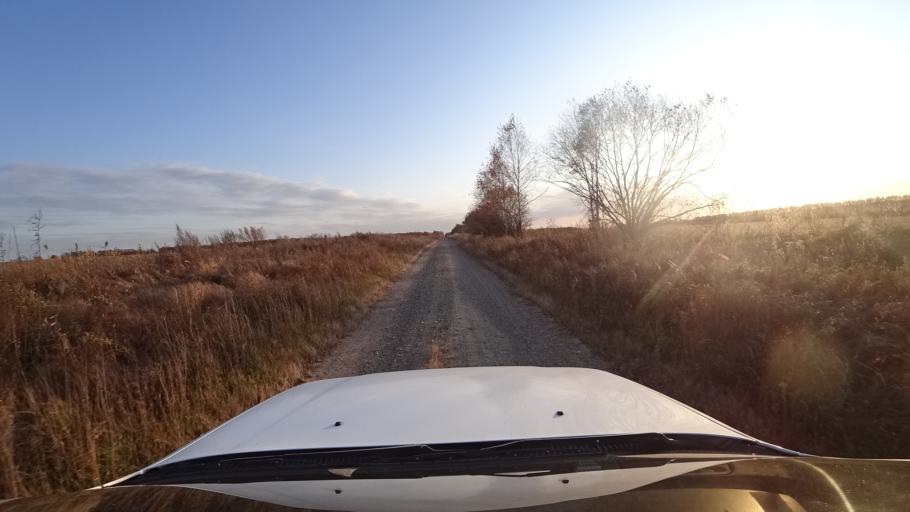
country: RU
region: Primorskiy
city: Lazo
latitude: 45.8125
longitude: 133.6091
